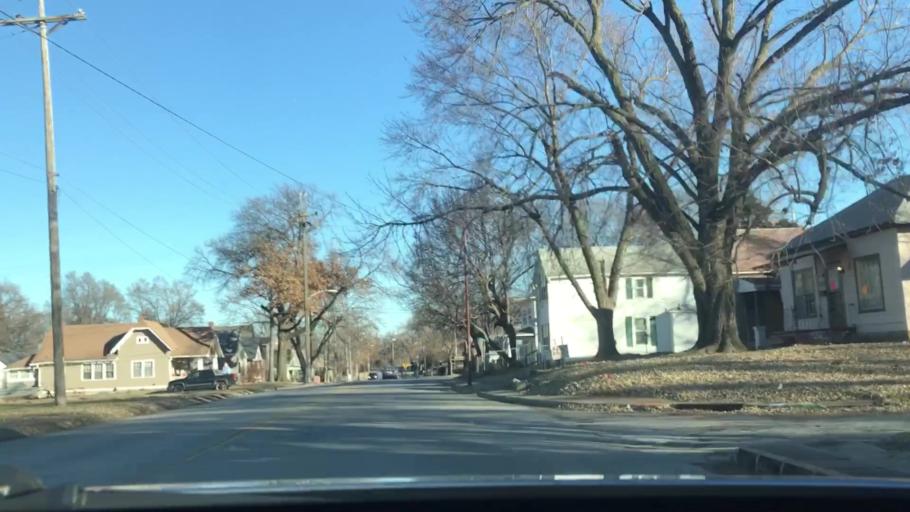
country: US
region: Kansas
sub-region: Johnson County
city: Roeland Park
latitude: 39.0729
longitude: -94.6499
